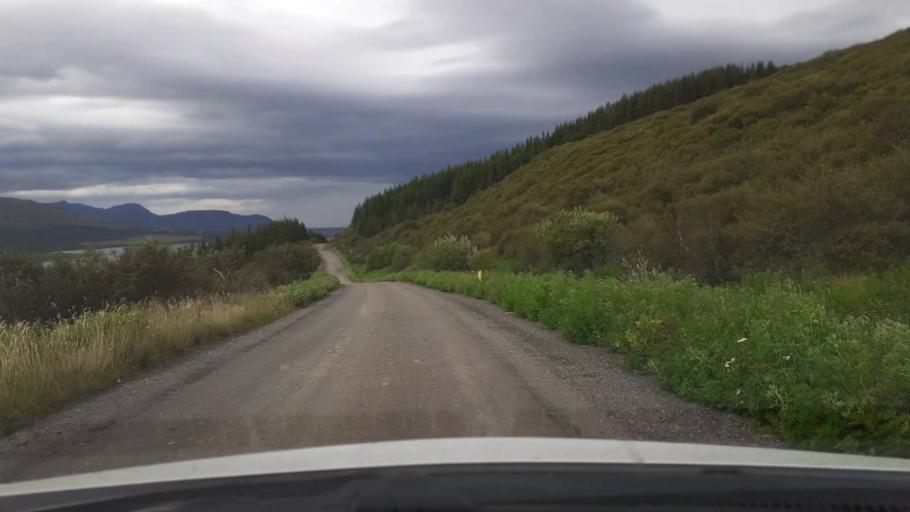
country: IS
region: Capital Region
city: Mosfellsbaer
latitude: 64.5275
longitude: -21.4939
